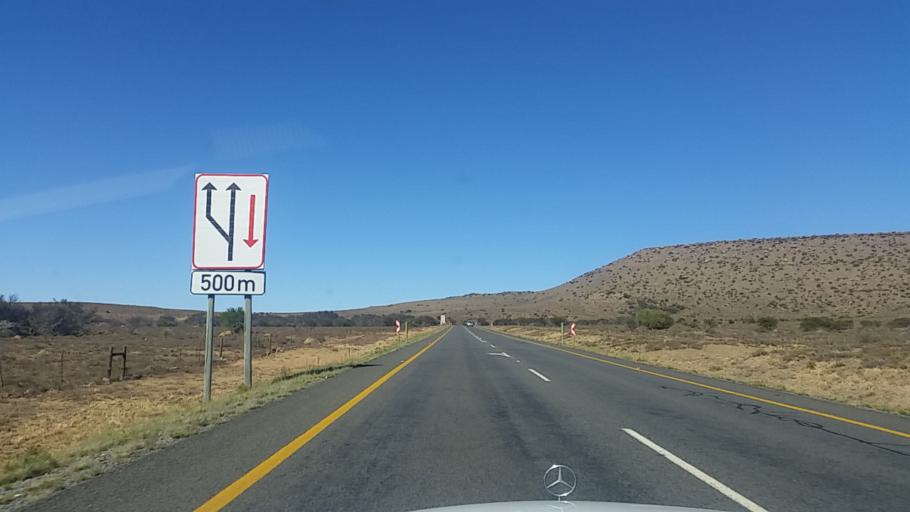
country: ZA
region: Eastern Cape
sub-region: Cacadu District Municipality
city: Graaff-Reinet
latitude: -31.9422
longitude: 24.7311
